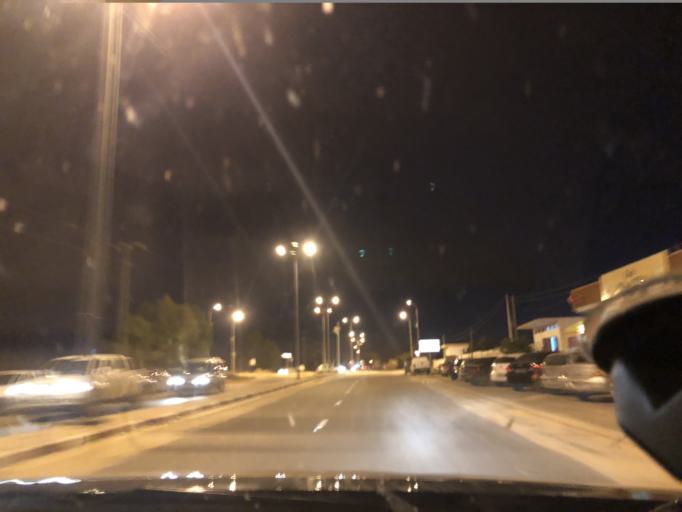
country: TN
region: Al Qasrayn
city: Kasserine
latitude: 35.1844
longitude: 8.8623
